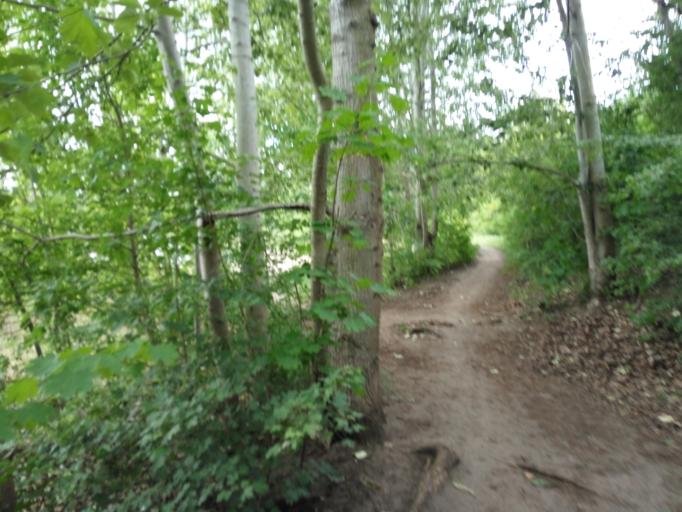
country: DE
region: Berlin
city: Kaulsdorf
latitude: 52.4948
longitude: 13.5932
